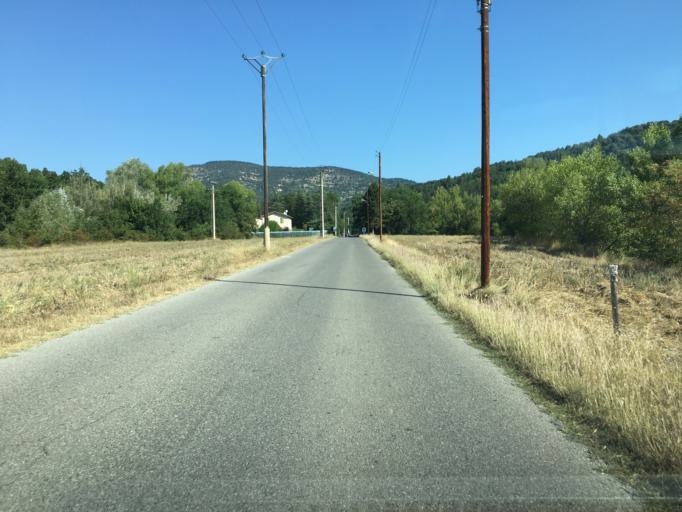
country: FR
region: Provence-Alpes-Cote d'Azur
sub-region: Departement des Alpes-de-Haute-Provence
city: Mallemoisson
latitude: 44.0559
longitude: 6.1491
